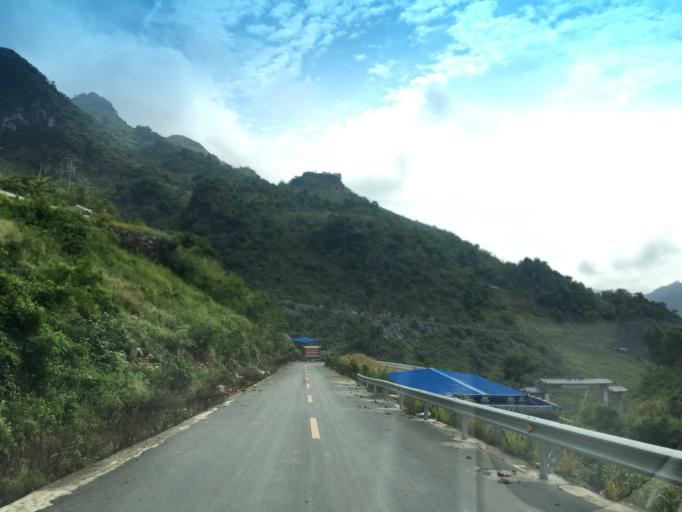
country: CN
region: Guangxi Zhuangzu Zizhiqu
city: Xinzhou
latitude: 24.8246
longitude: 105.6459
